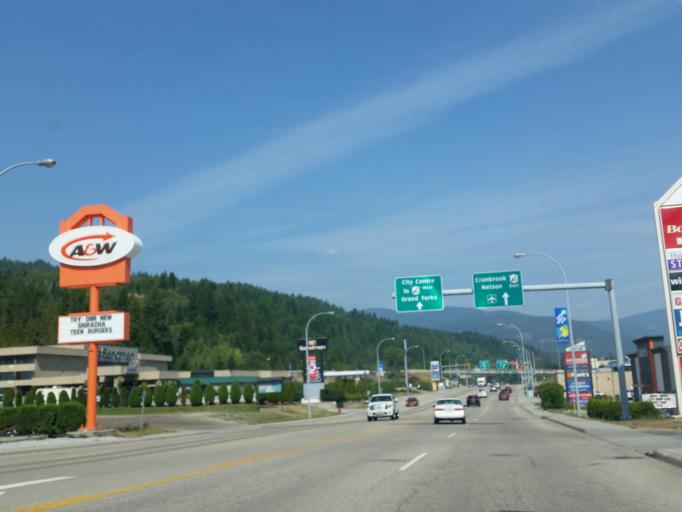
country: CA
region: British Columbia
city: Castlegar
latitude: 49.2956
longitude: -117.6536
